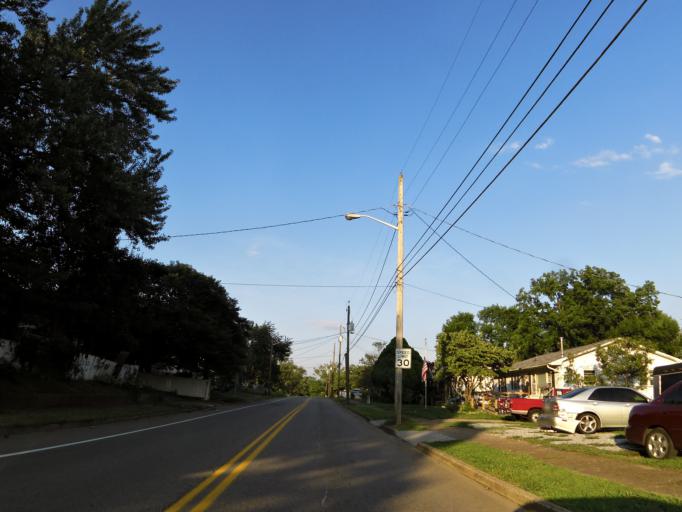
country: US
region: Tennessee
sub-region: Knox County
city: Knoxville
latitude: 35.9735
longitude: -83.9509
